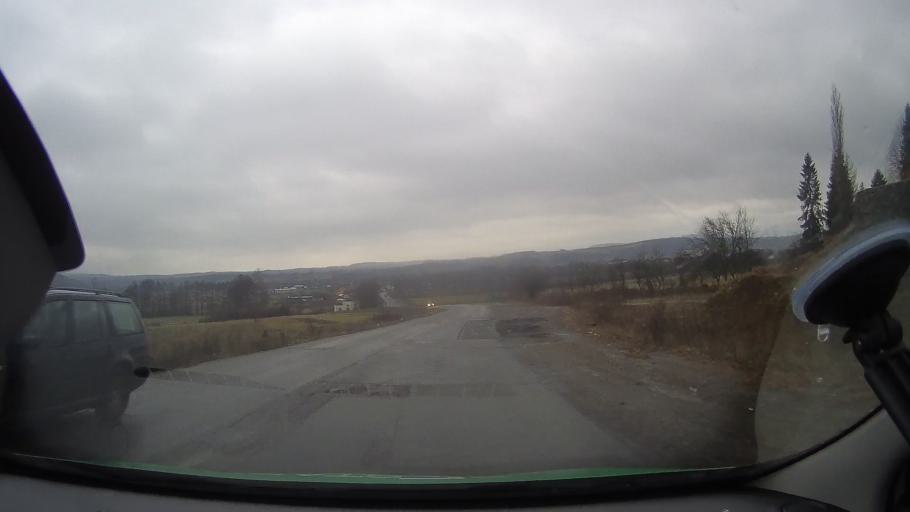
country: RO
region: Arad
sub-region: Comuna Halmagiu
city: Halmagiu
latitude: 46.2768
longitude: 22.5932
